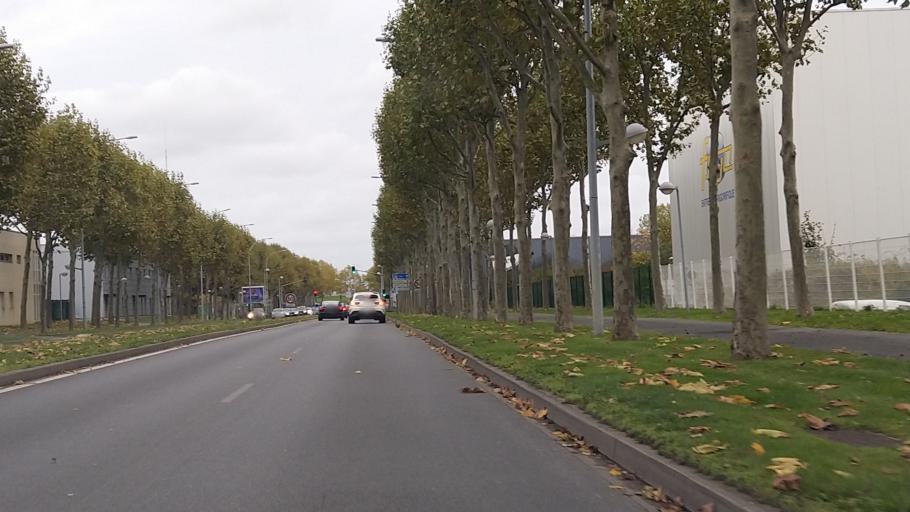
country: FR
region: Ile-de-France
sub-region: Departement de l'Essonne
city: Fleury-Merogis
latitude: 48.6485
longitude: 2.3760
